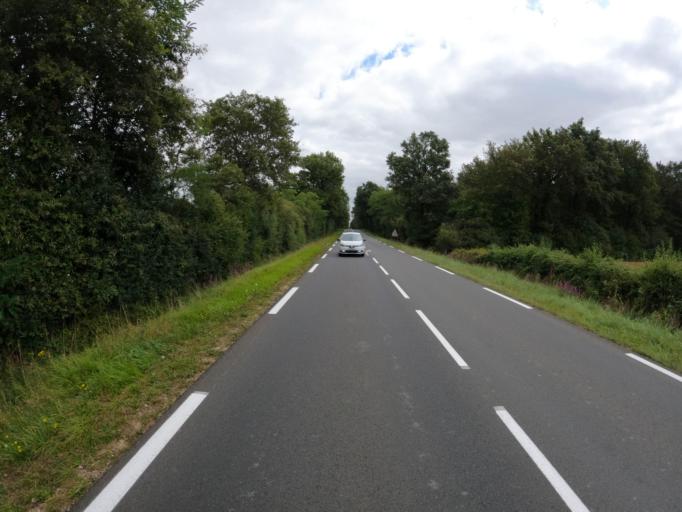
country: FR
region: Poitou-Charentes
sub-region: Departement de la Vienne
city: Charroux
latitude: 46.1259
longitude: 0.4959
